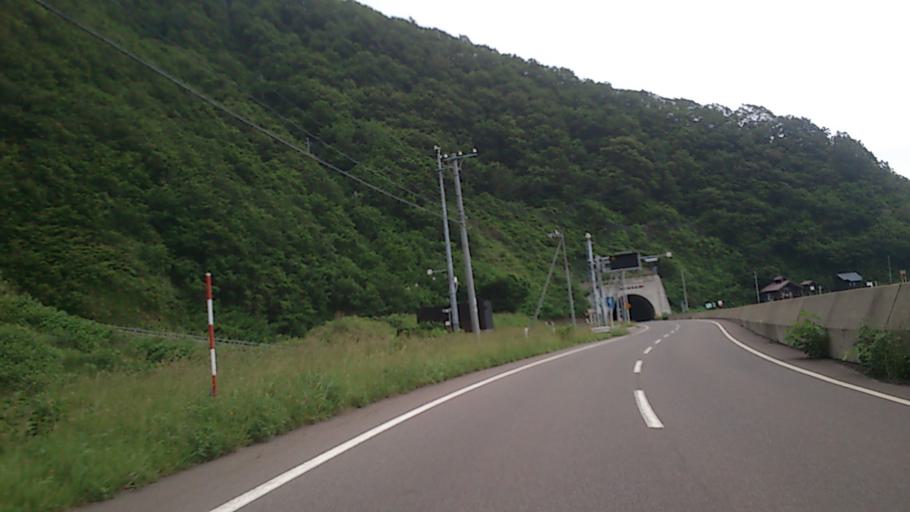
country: JP
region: Hokkaido
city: Kamiiso
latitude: 42.2699
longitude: 139.7846
